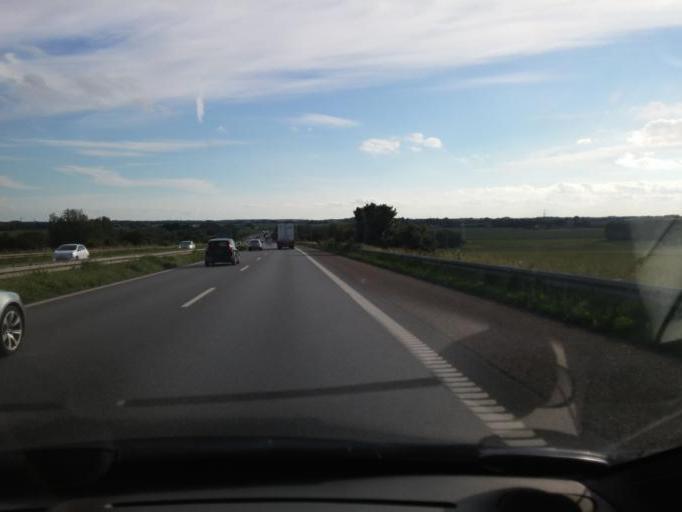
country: DK
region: Zealand
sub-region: Slagelse Kommune
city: Forlev
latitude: 55.3749
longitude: 11.3065
